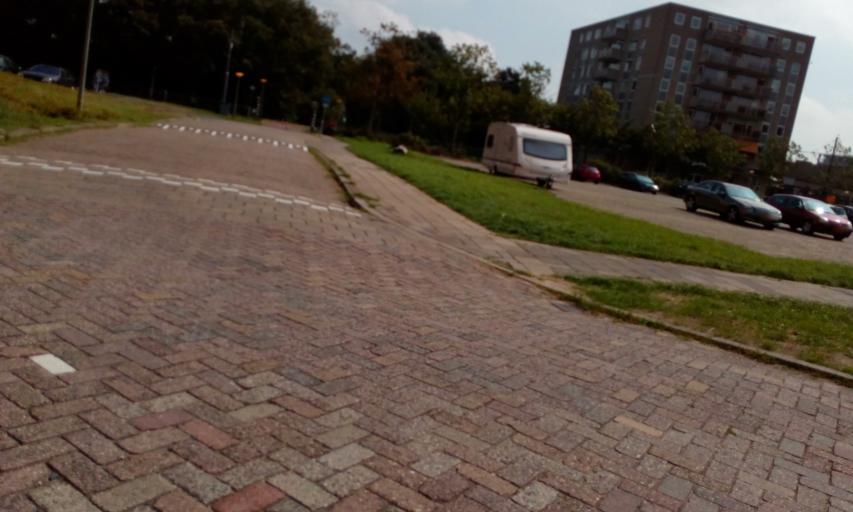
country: NL
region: South Holland
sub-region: Gemeente Schiedam
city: Schiedam
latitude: 51.9357
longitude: 4.3732
